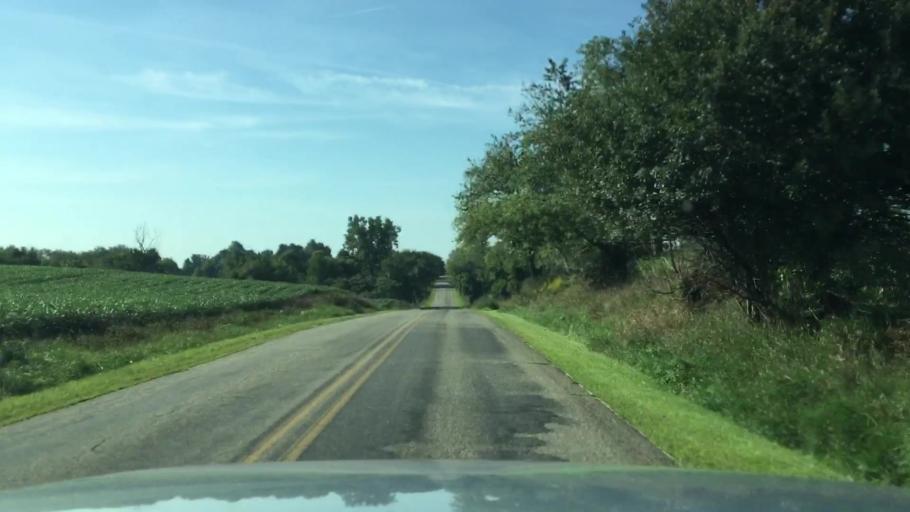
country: US
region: Michigan
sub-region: Lenawee County
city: Hudson
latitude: 41.9183
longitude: -84.4205
